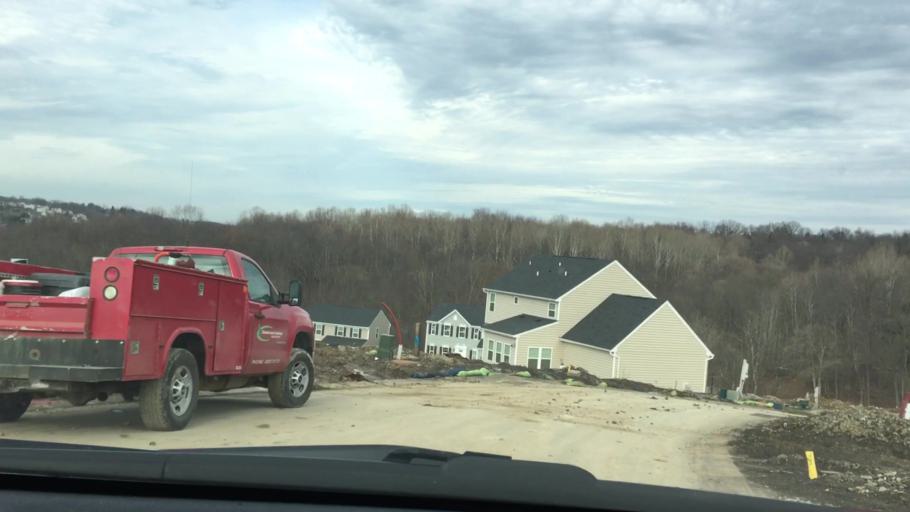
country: US
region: Pennsylvania
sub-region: Allegheny County
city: South Park Township
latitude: 40.2986
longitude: -79.9692
